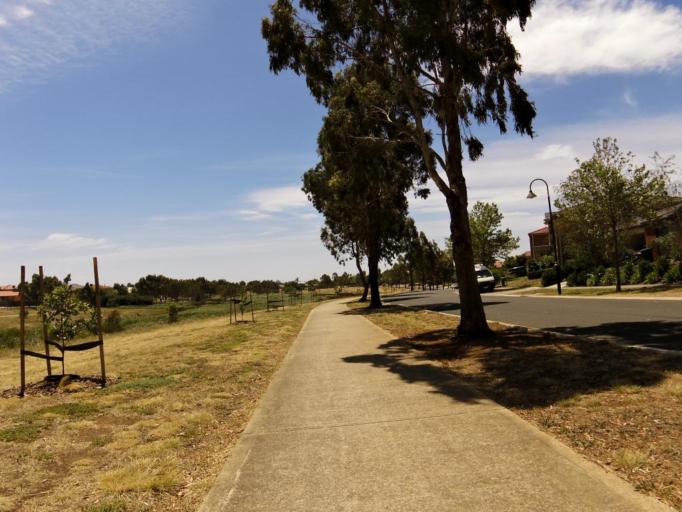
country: AU
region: Victoria
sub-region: Wyndham
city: Williams Landing
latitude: -37.8566
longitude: 144.7149
